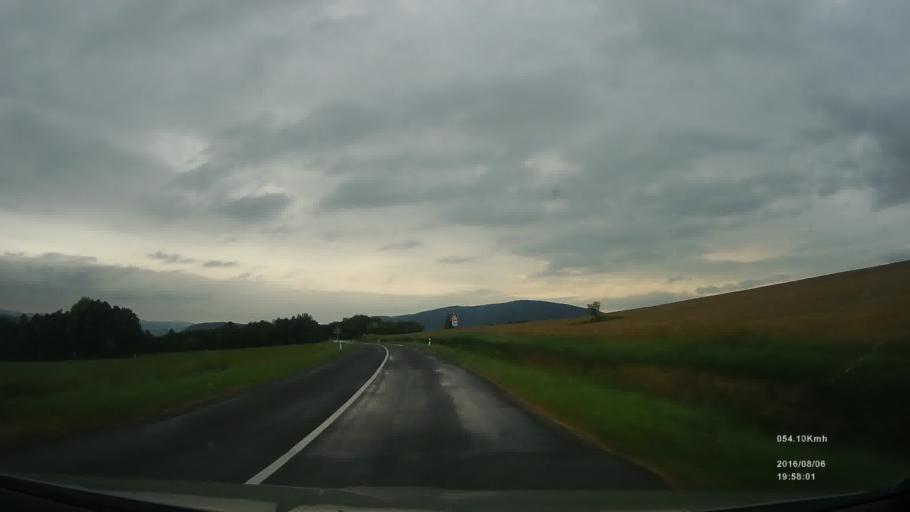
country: SK
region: Presovsky
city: Svidnik
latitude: 49.2721
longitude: 21.5792
